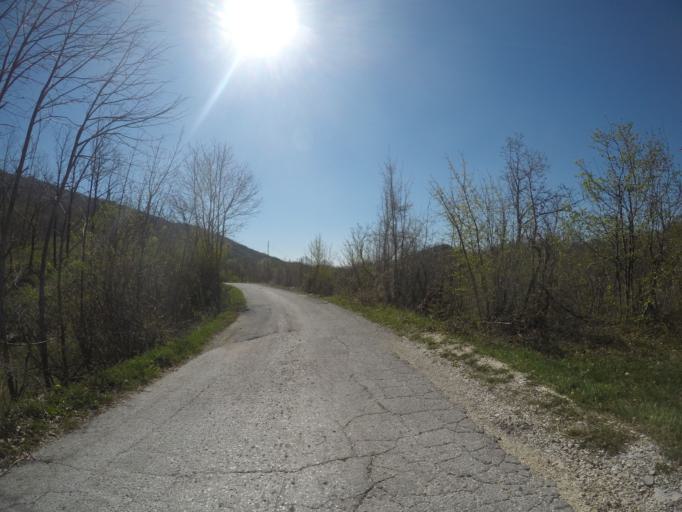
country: ME
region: Danilovgrad
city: Danilovgrad
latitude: 42.5395
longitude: 19.0106
